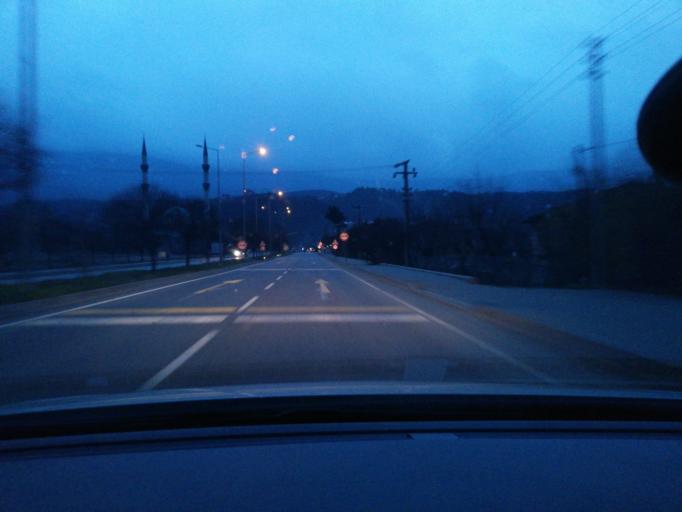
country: TR
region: Bolu
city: Bolu
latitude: 40.6917
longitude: 31.6196
